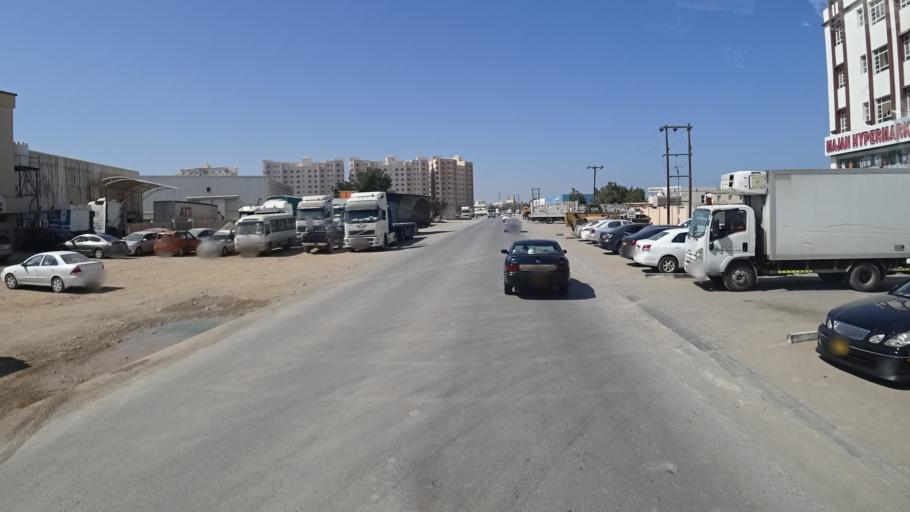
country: OM
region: Muhafazat Masqat
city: Bawshar
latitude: 23.5753
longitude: 58.3700
